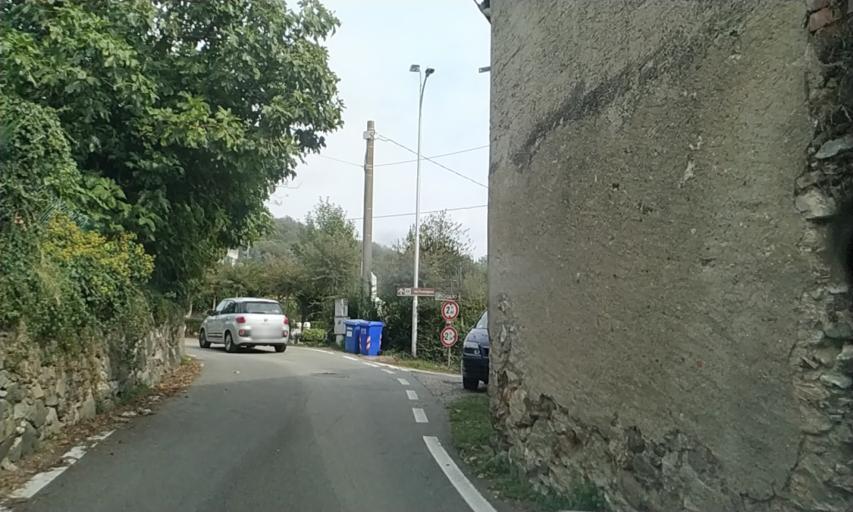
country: IT
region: Piedmont
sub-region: Provincia di Biella
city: Roppolo
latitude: 45.4212
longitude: 8.0747
